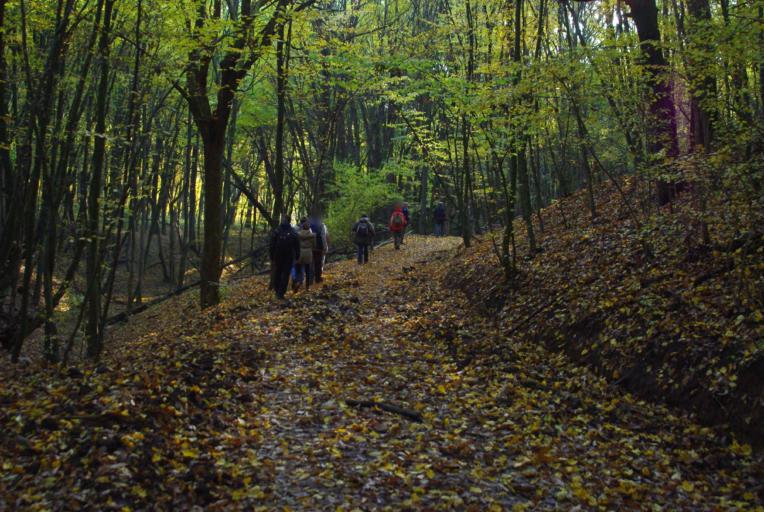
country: HU
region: Pest
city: Nagymaros
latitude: 47.8174
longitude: 18.9353
